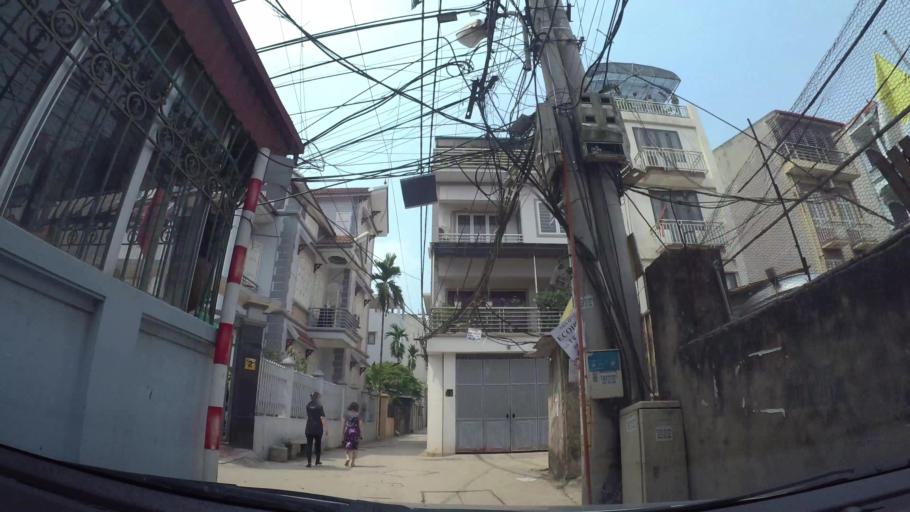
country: VN
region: Ha Noi
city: Tay Ho
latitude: 21.0874
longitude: 105.8002
